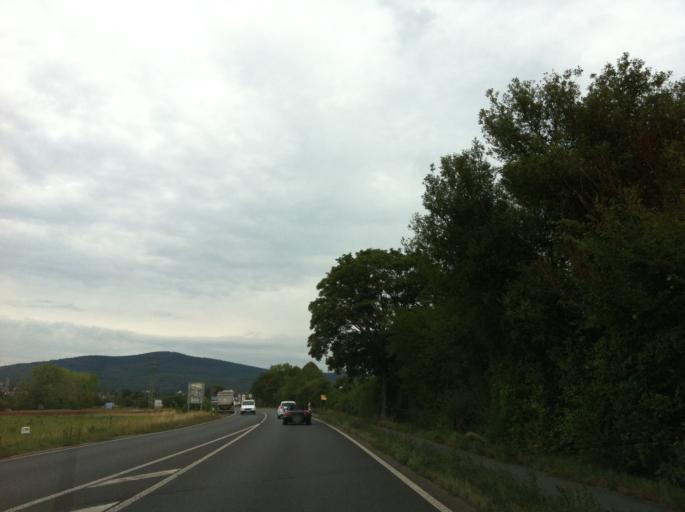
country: DE
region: Hesse
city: Schwalbach am Taunus
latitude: 50.1650
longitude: 8.5346
